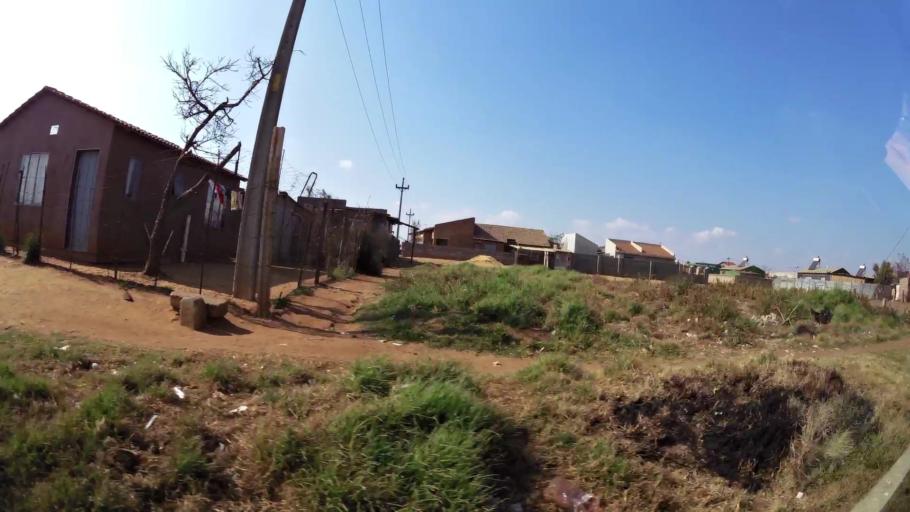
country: ZA
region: Gauteng
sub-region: Ekurhuleni Metropolitan Municipality
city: Springs
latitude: -26.1161
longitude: 28.4803
